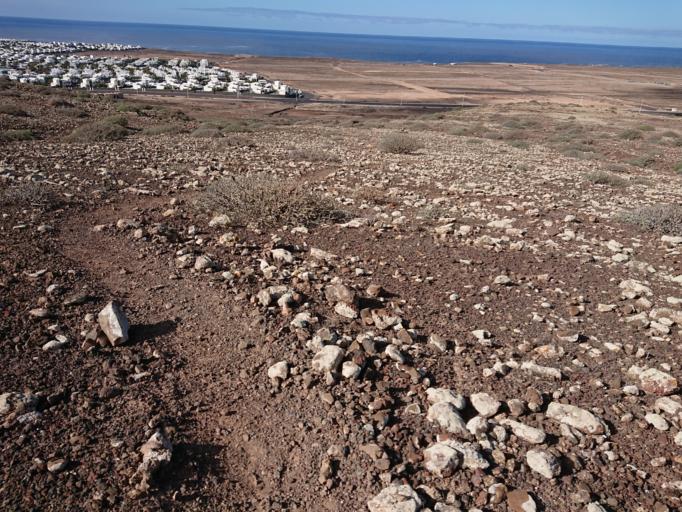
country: ES
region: Canary Islands
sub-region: Provincia de Las Palmas
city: Playa Blanca
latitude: 28.8724
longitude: -13.8595
